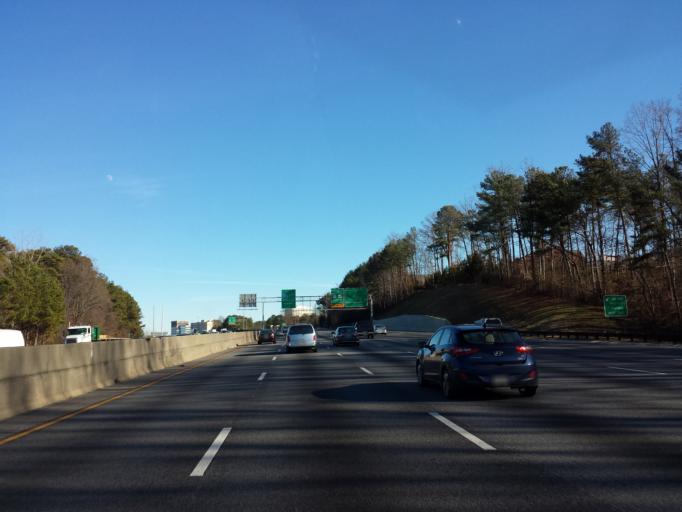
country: US
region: Georgia
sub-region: Fulton County
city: Sandy Springs
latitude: 33.9104
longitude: -84.3674
